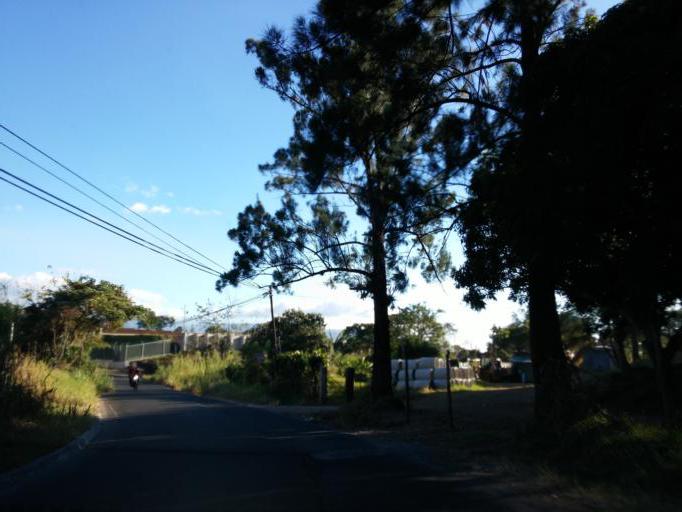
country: CR
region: Heredia
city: Llorente
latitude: 10.0150
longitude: -84.1730
